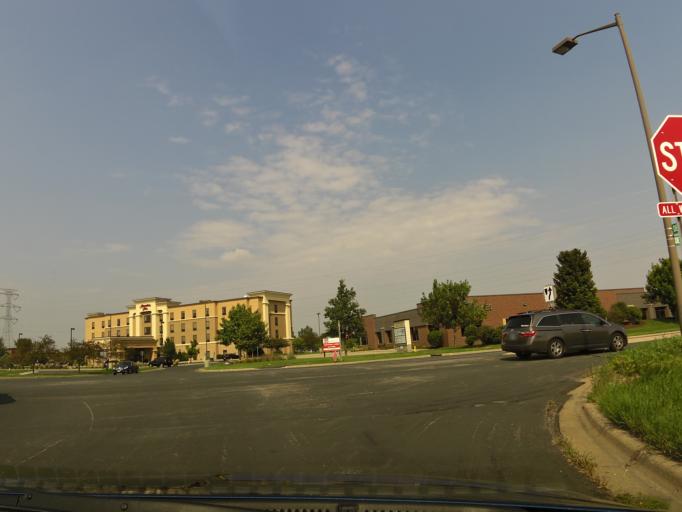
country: US
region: Minnesota
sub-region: Scott County
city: Shakopee
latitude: 44.7794
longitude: -93.4659
